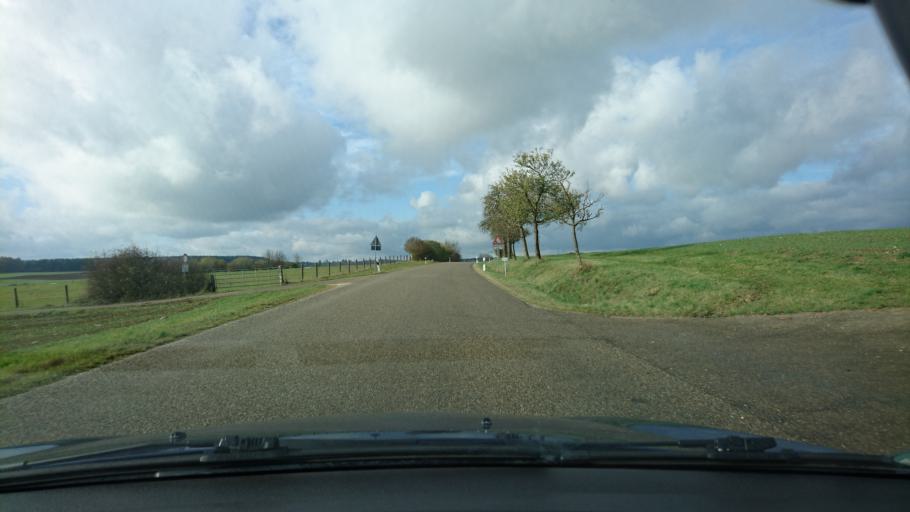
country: DE
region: Bavaria
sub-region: Swabia
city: Forheim
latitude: 48.7518
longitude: 10.4613
